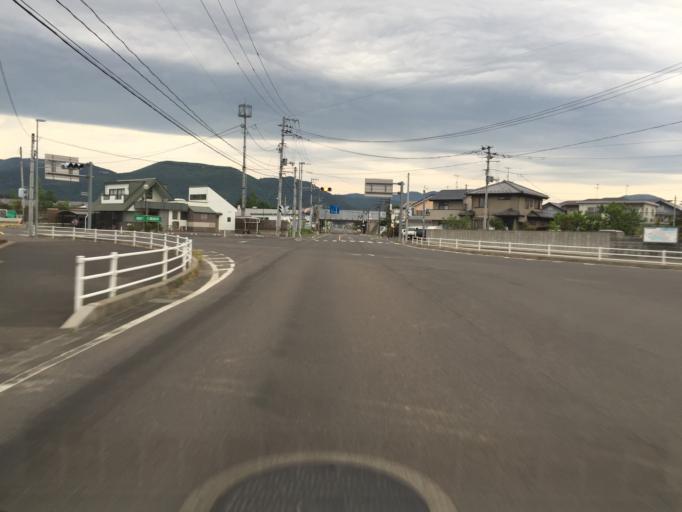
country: JP
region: Fukushima
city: Fukushima-shi
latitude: 37.7950
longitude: 140.4311
